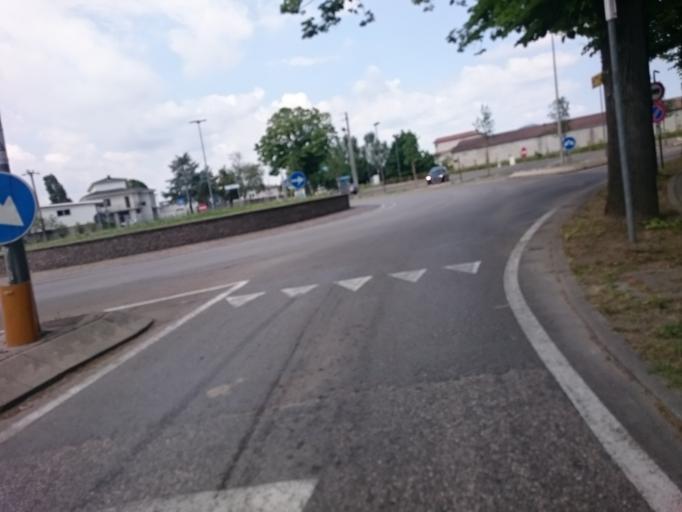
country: IT
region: Veneto
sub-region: Provincia di Padova
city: Carceri
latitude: 45.1964
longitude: 11.6213
